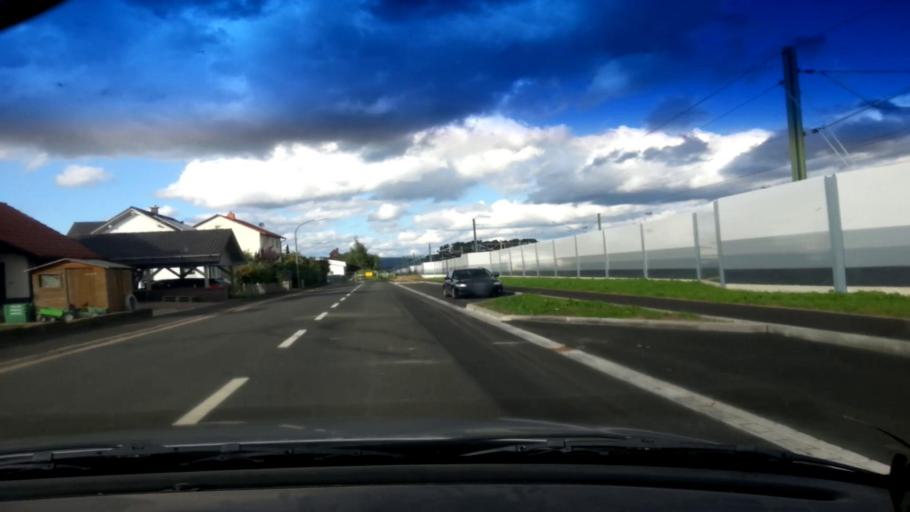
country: DE
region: Bavaria
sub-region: Upper Franconia
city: Ebensfeld
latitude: 50.0689
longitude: 10.9543
